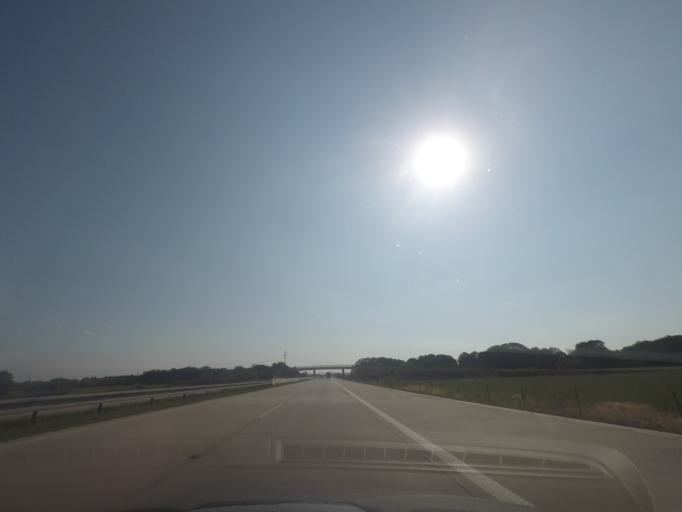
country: CZ
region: Moravskoslezsky
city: Bohumin
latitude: 49.9240
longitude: 18.3811
